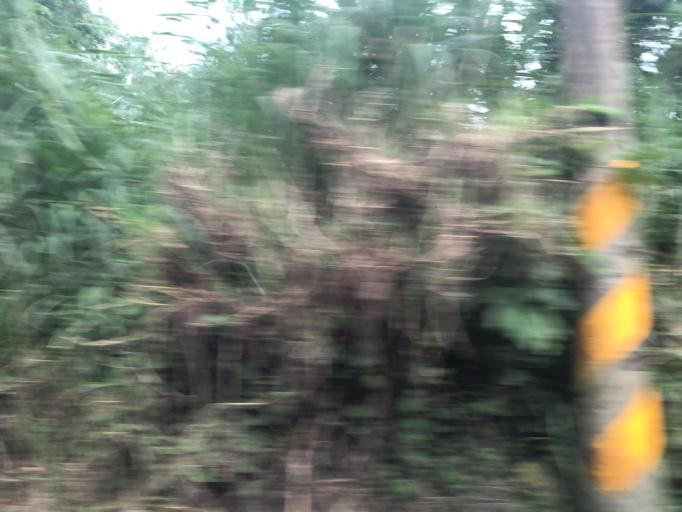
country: TW
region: Taiwan
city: Daxi
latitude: 24.9182
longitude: 121.3537
